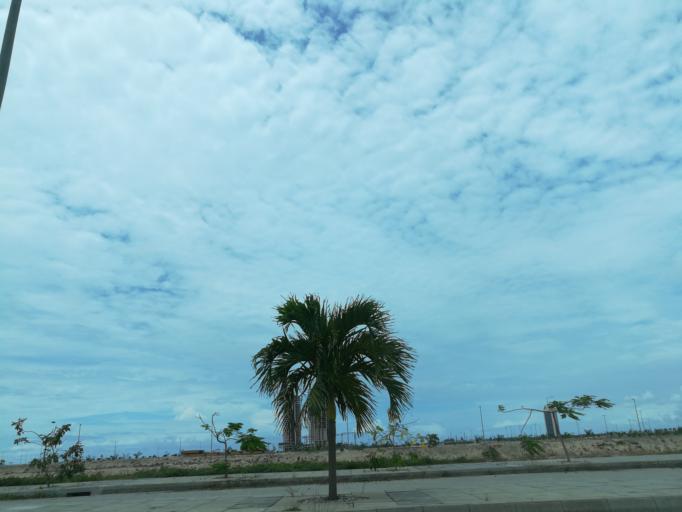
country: NG
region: Lagos
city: Ikoyi
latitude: 6.4072
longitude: 3.4165
